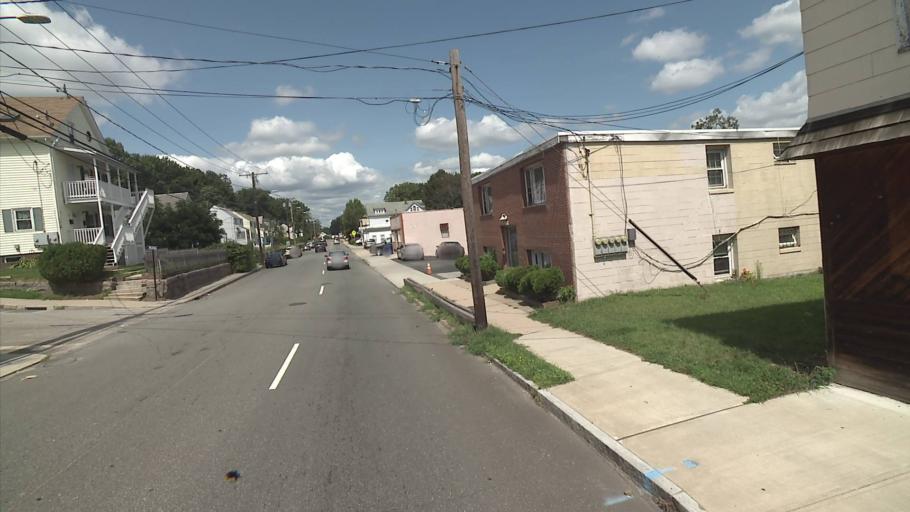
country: US
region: Connecticut
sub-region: New London County
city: New London
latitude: 41.3542
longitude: -72.1106
